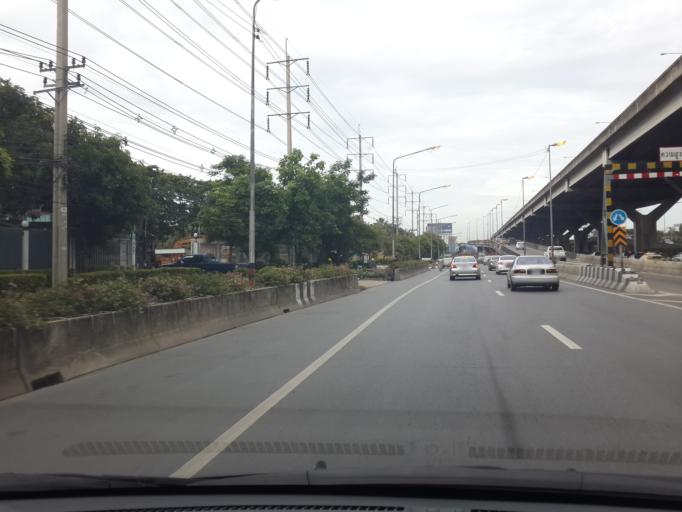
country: TH
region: Bangkok
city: Lak Si
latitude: 13.8713
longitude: 100.5744
